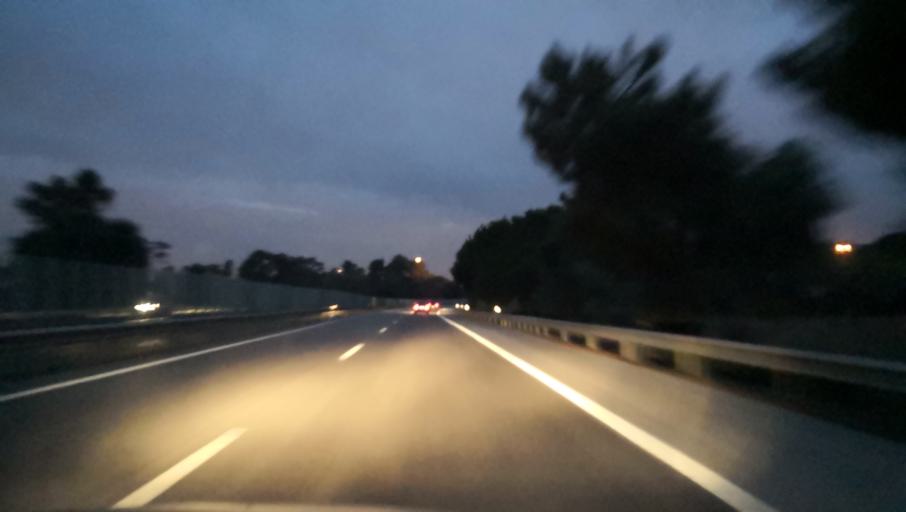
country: PT
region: Setubal
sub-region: Barreiro
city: Santo Antonio da Charneca
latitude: 38.6298
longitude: -9.0401
